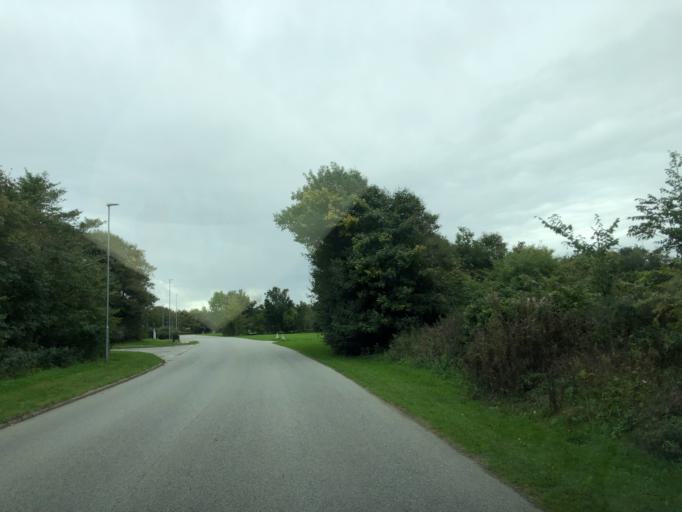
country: DK
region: North Denmark
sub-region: Thisted Kommune
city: Thisted
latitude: 56.9684
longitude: 8.6924
